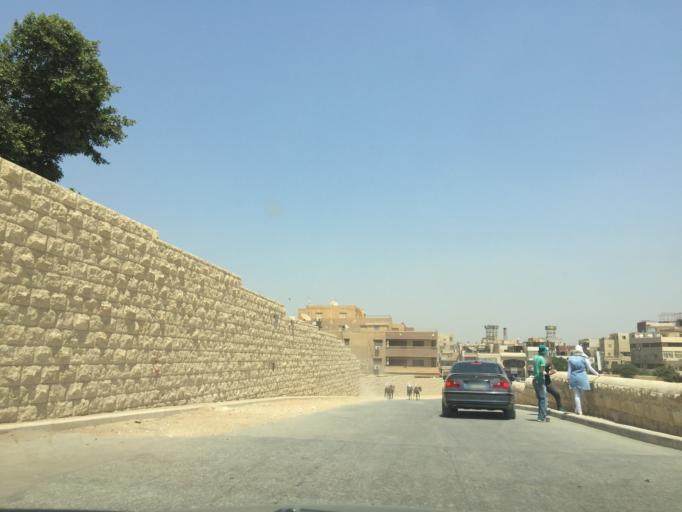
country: EG
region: Al Jizah
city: Al Jizah
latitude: 29.9758
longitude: 31.1390
